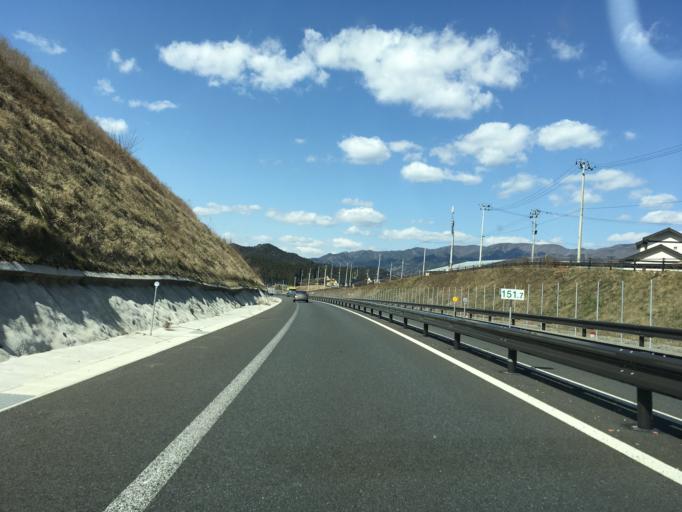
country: JP
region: Iwate
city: Ofunato
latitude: 38.9997
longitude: 141.6148
